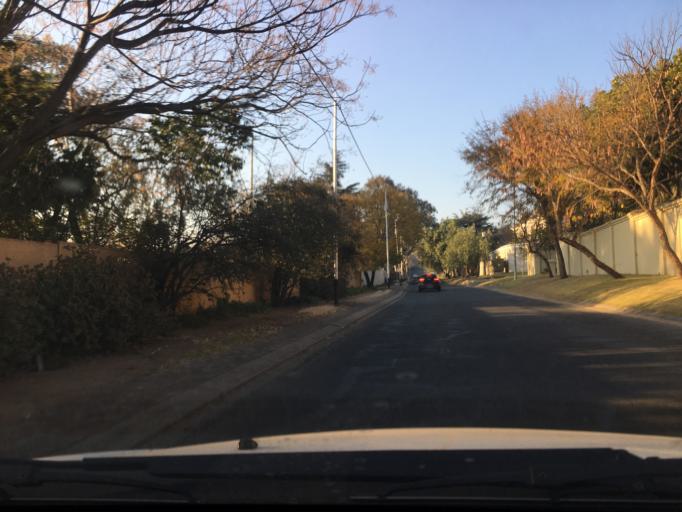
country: ZA
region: Gauteng
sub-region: City of Johannesburg Metropolitan Municipality
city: Diepsloot
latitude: -26.0681
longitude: 28.0079
